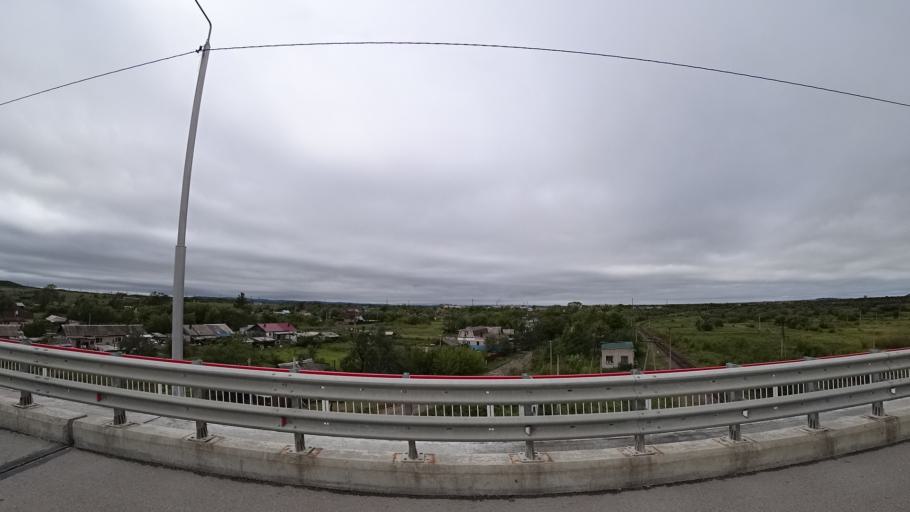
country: RU
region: Primorskiy
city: Monastyrishche
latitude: 44.1916
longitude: 132.4417
